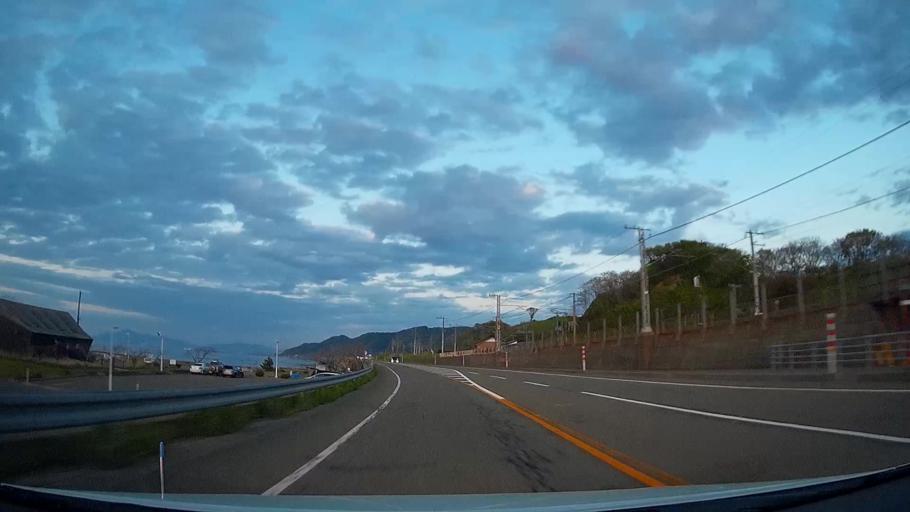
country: JP
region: Niigata
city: Joetsu
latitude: 37.1636
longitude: 138.1410
